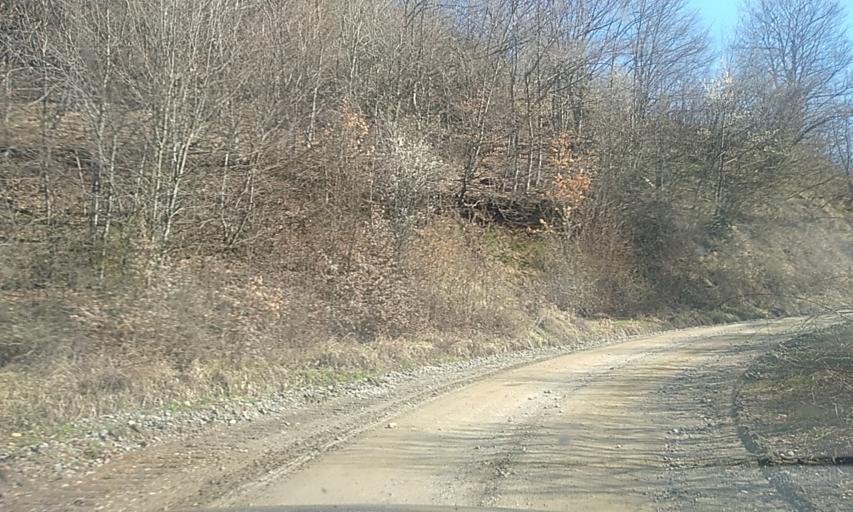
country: MK
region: Kriva Palanka
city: Kriva Palanka
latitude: 42.3424
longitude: 22.3612
